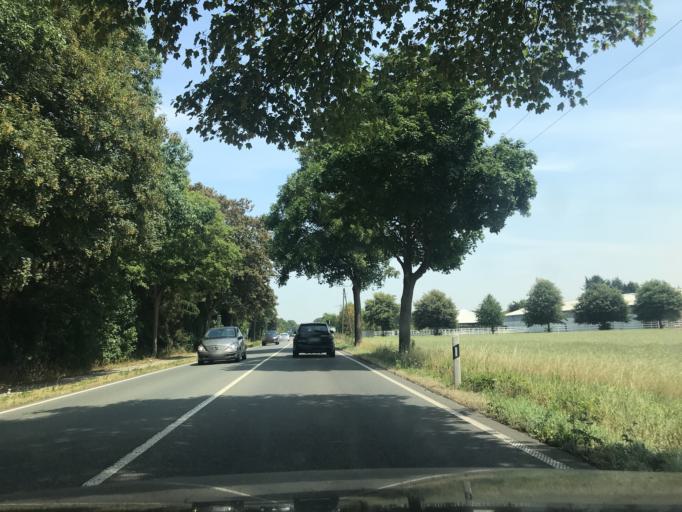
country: DE
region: North Rhine-Westphalia
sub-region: Regierungsbezirk Dusseldorf
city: Alpen
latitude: 51.5629
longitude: 6.4860
